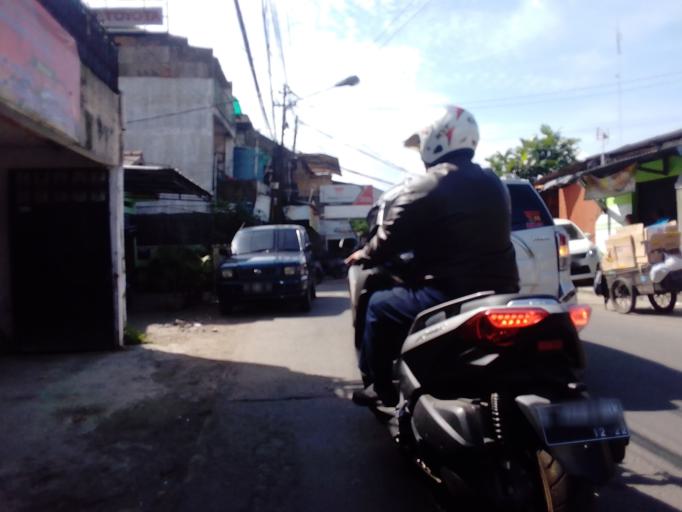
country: ID
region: West Java
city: Bandung
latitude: -6.9441
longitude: 107.6633
